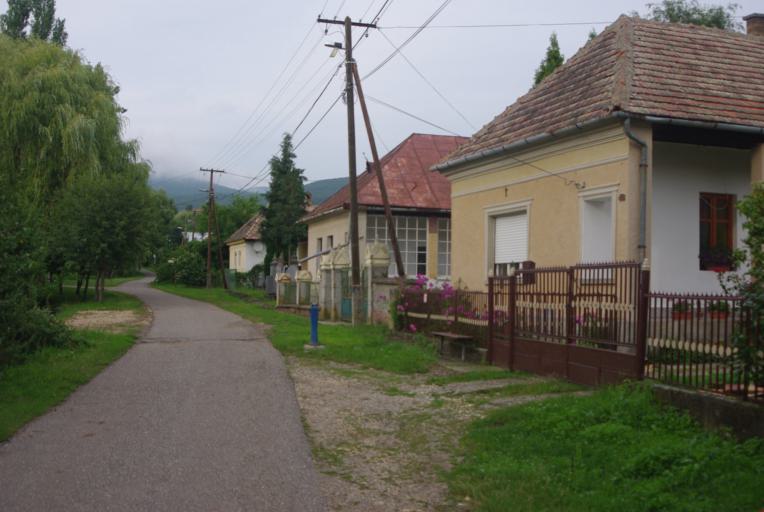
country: HU
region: Borsod-Abauj-Zemplen
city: Gonc
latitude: 48.3885
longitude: 21.2838
